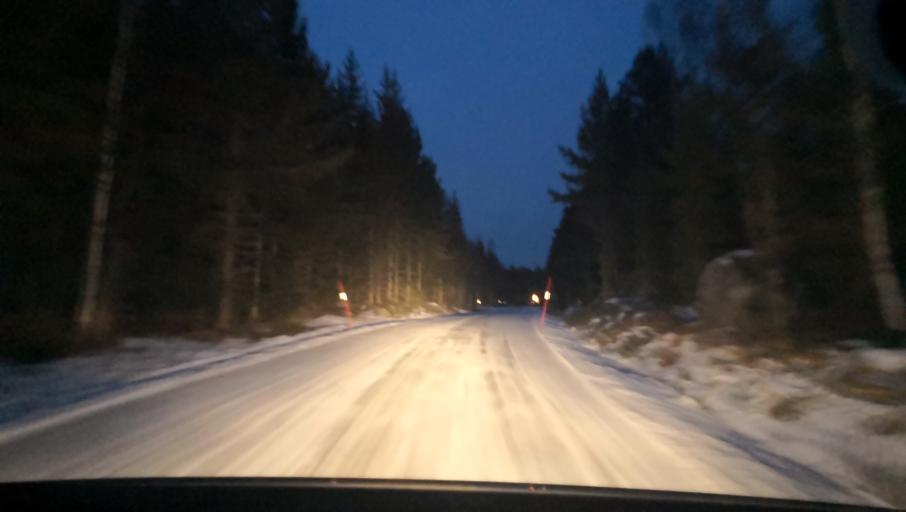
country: SE
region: Uppsala
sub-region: Heby Kommun
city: Tarnsjo
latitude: 60.2502
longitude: 16.7311
